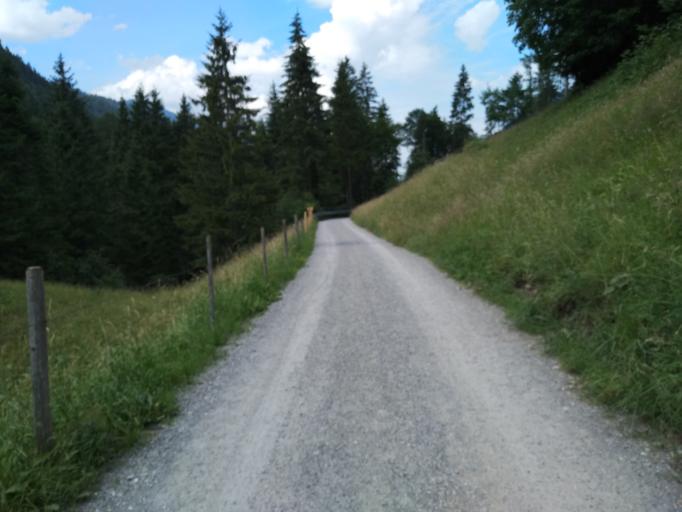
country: AT
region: Tyrol
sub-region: Politischer Bezirk Reutte
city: Steeg
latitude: 47.3176
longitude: 10.2663
